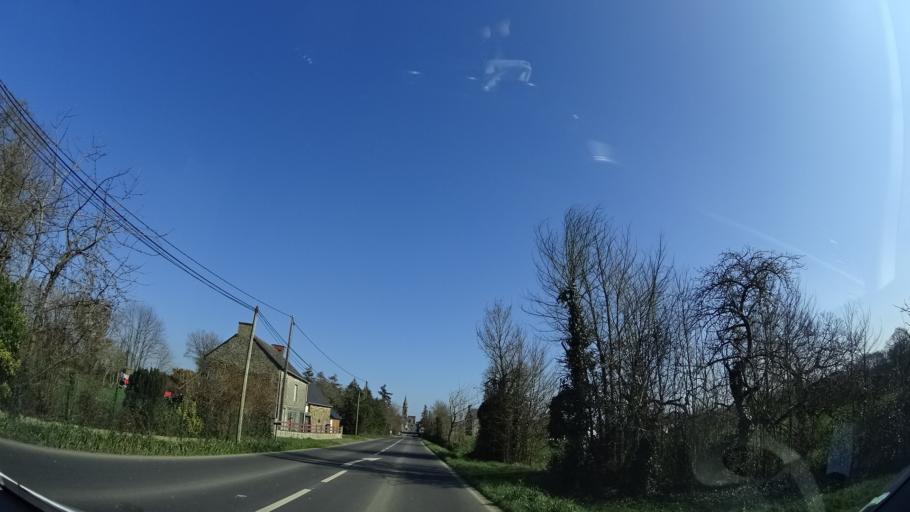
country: FR
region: Brittany
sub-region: Departement d'Ille-et-Vilaine
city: Meillac
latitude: 48.4125
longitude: -1.8204
